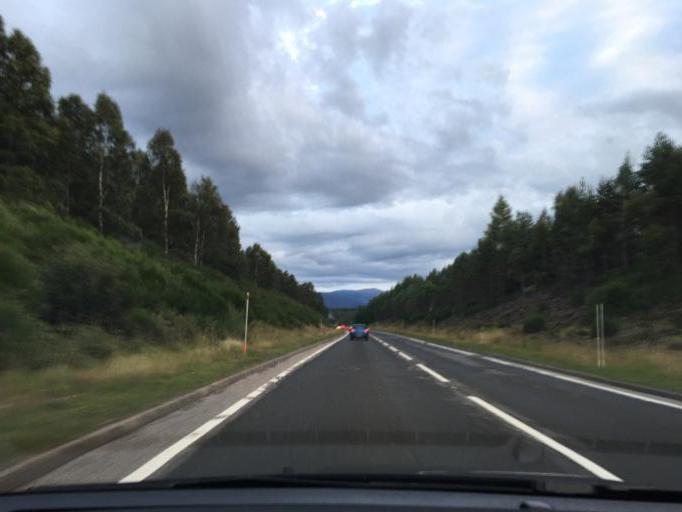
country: GB
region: Scotland
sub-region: Highland
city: Aviemore
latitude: 57.2883
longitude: -3.8447
